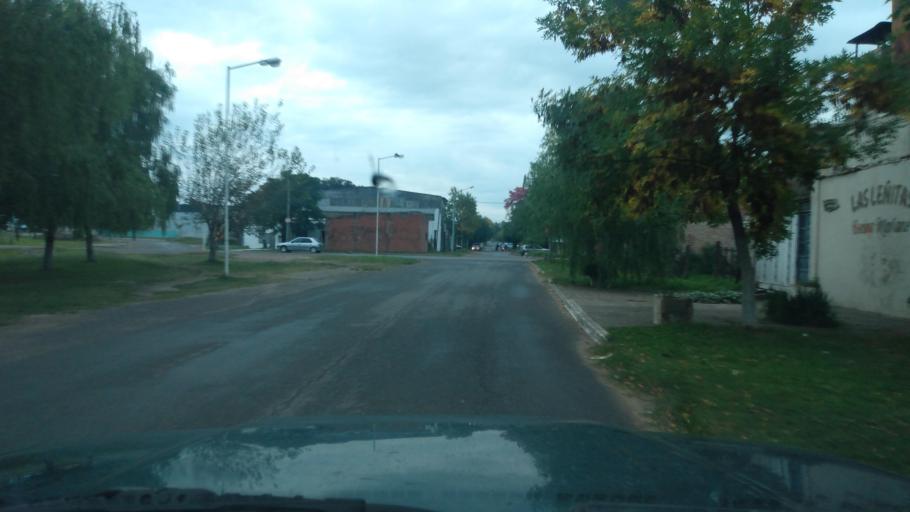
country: AR
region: Buenos Aires
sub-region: Partido de Lujan
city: Lujan
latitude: -34.5616
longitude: -59.0872
